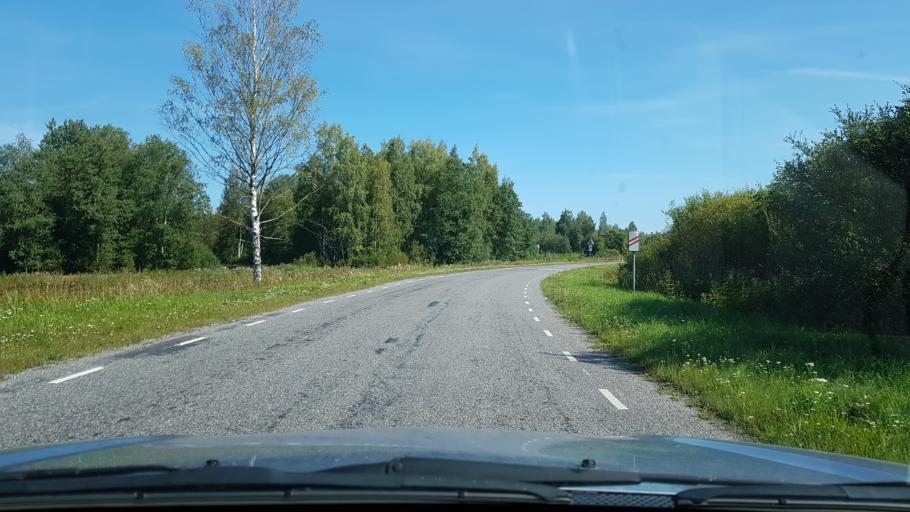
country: EE
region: Ida-Virumaa
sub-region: Sillamaee linn
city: Sillamae
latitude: 59.3474
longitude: 27.7298
